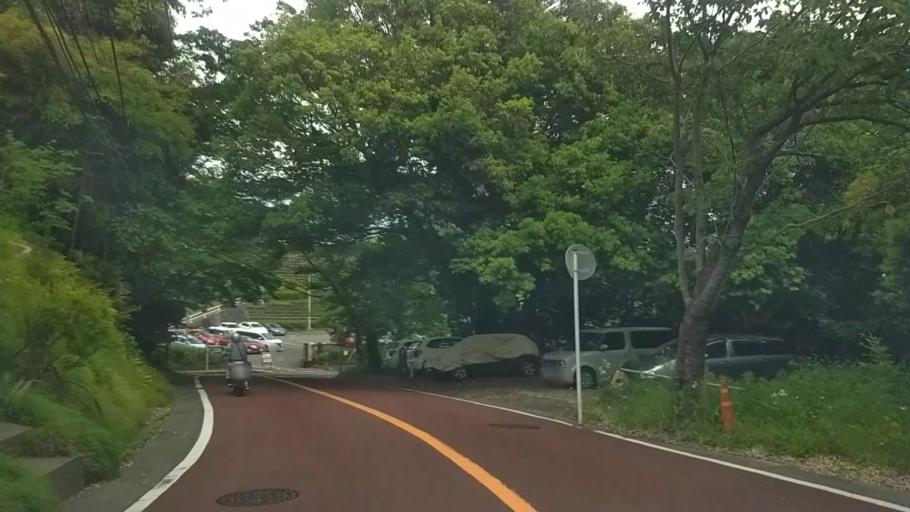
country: JP
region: Kanagawa
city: Kamakura
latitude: 35.3221
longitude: 139.5232
